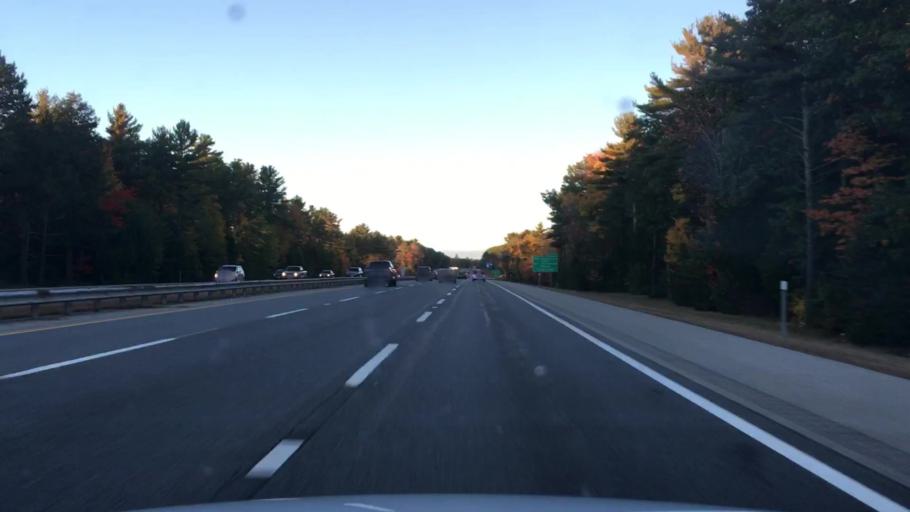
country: US
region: Maine
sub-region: York County
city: Wells Beach Station
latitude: 43.3001
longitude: -70.6155
